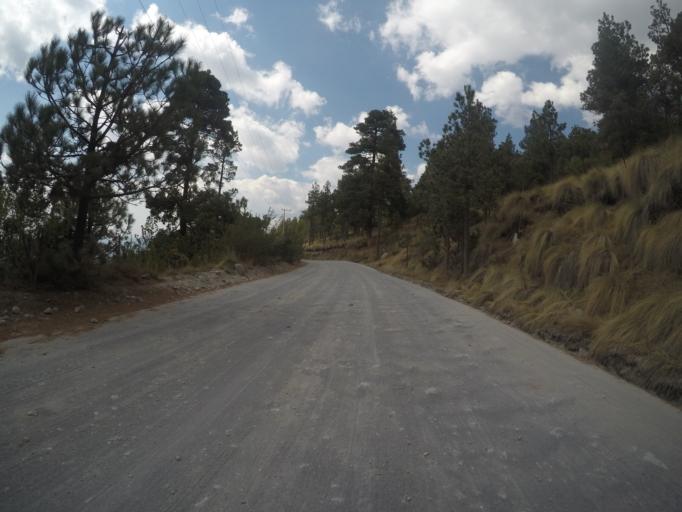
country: MX
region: Mexico
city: Cerro La Calera
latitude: 19.1425
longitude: -99.8016
